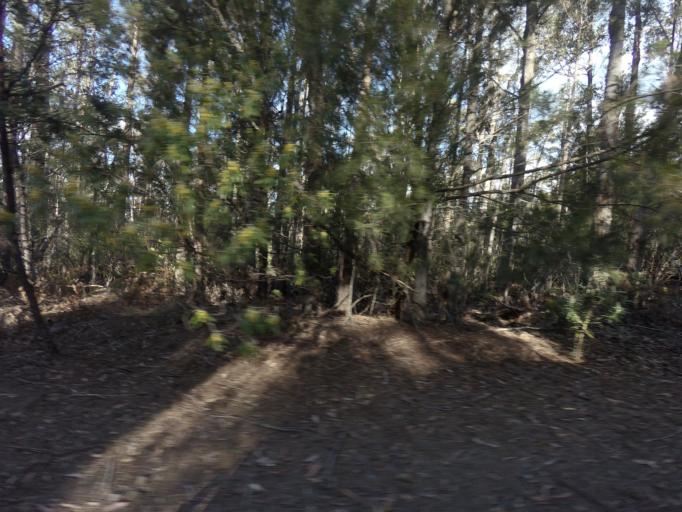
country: AU
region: Tasmania
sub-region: Break O'Day
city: St Helens
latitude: -41.8429
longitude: 148.0620
